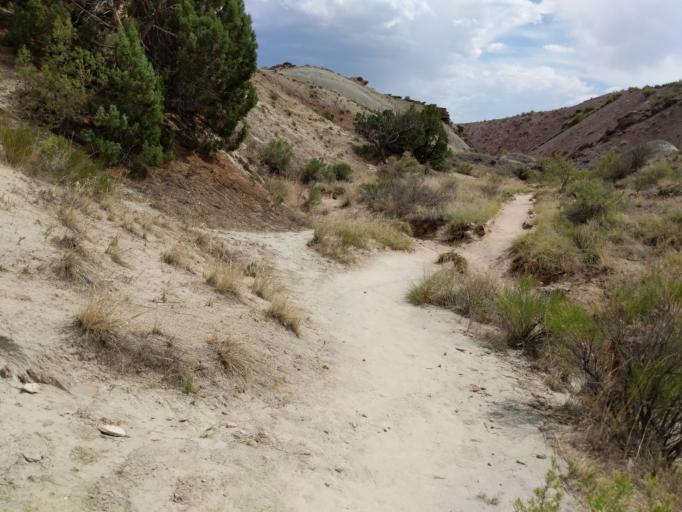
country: US
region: Utah
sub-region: Uintah County
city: Naples
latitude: 40.4418
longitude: -109.2993
